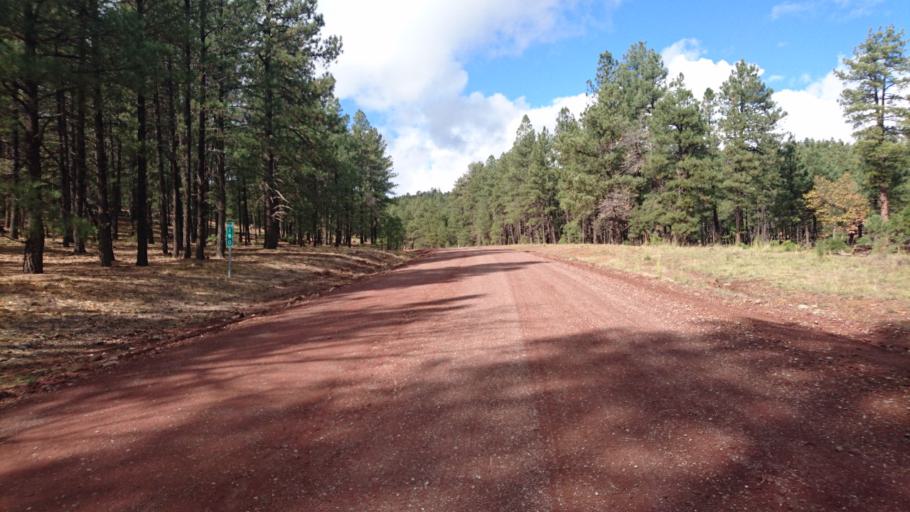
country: US
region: Arizona
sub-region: Coconino County
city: Parks
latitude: 35.2749
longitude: -111.8983
